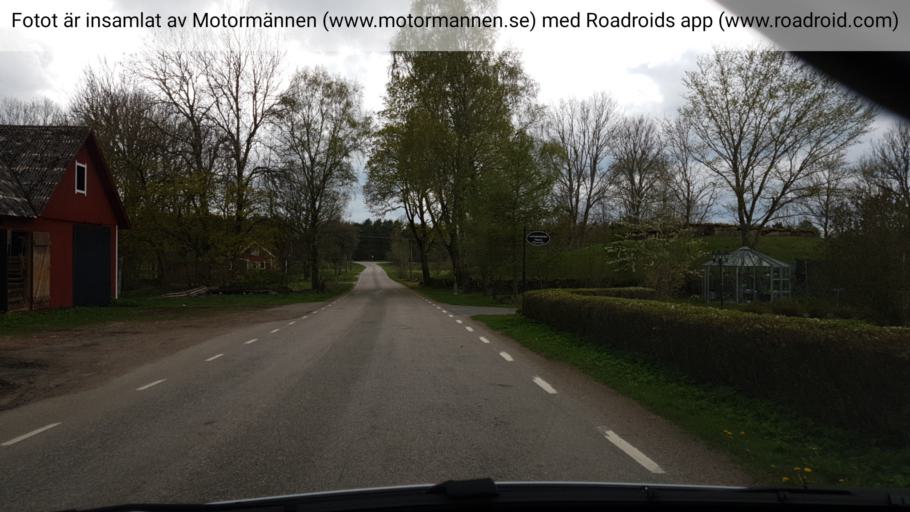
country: SE
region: Vaestra Goetaland
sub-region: Falkopings Kommun
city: Floby
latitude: 58.1853
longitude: 13.3482
